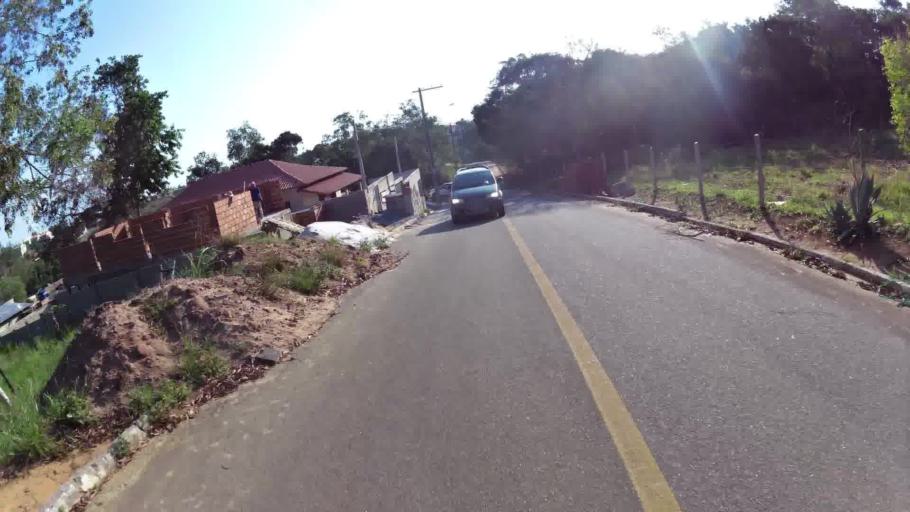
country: BR
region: Espirito Santo
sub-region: Guarapari
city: Guarapari
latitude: -20.7217
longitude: -40.5378
